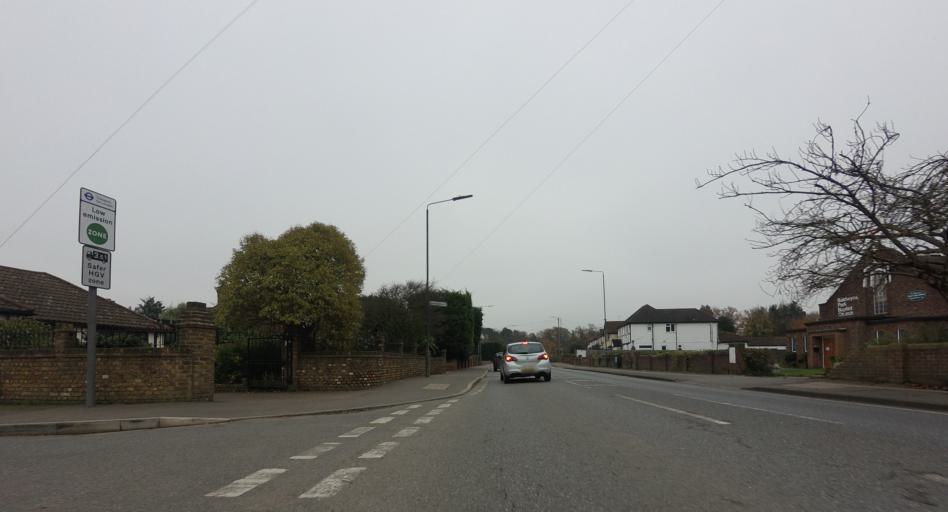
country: GB
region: England
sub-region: Greater London
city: Bexley
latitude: 51.4365
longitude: 0.1646
